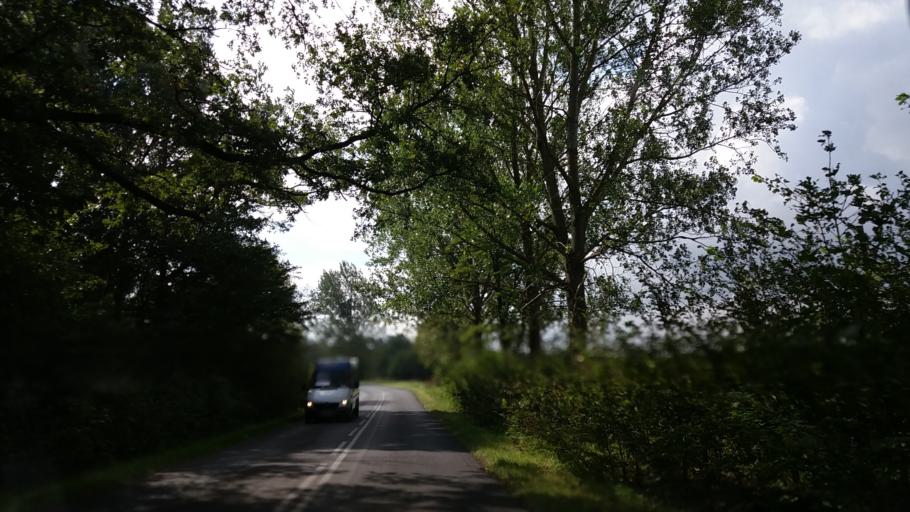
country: PL
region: West Pomeranian Voivodeship
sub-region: Powiat choszczenski
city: Choszczno
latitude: 53.1243
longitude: 15.4521
